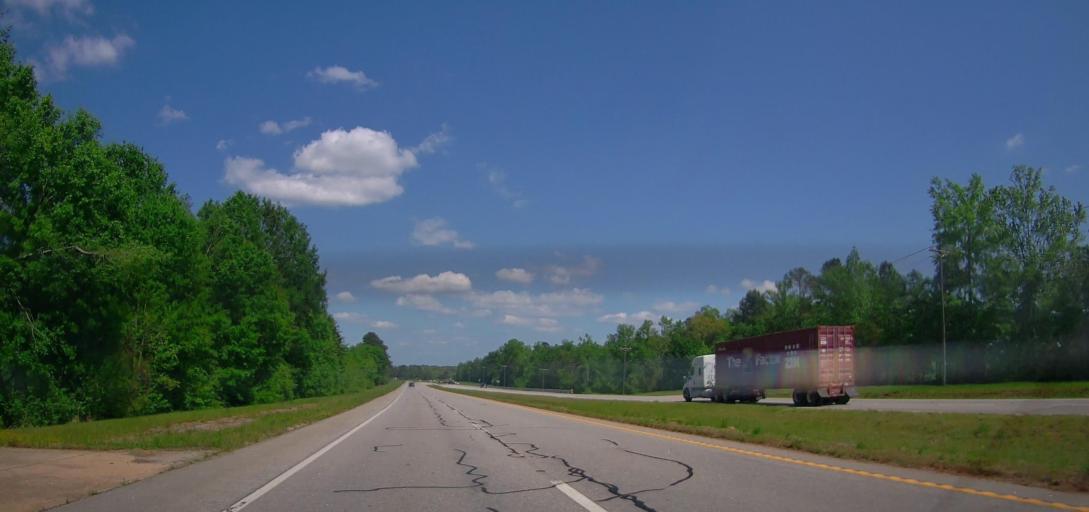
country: US
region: Georgia
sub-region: Putnam County
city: Eatonton
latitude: 33.2731
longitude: -83.3583
